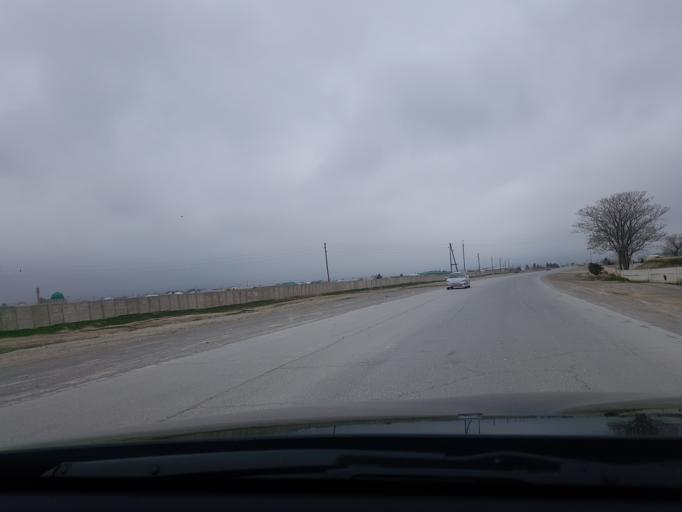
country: TM
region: Ahal
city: Arcabil
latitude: 38.1343
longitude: 57.9481
